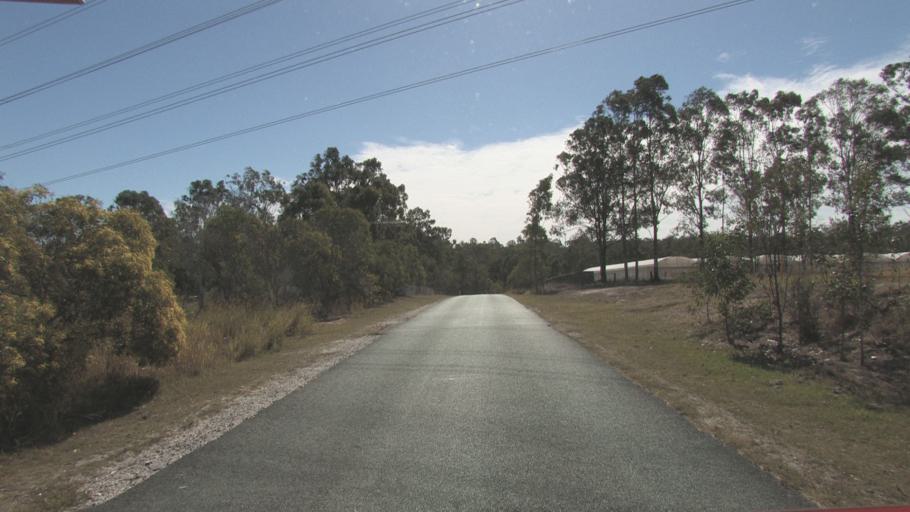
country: AU
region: Queensland
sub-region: Ipswich
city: Springfield Lakes
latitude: -27.7182
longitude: 152.9302
